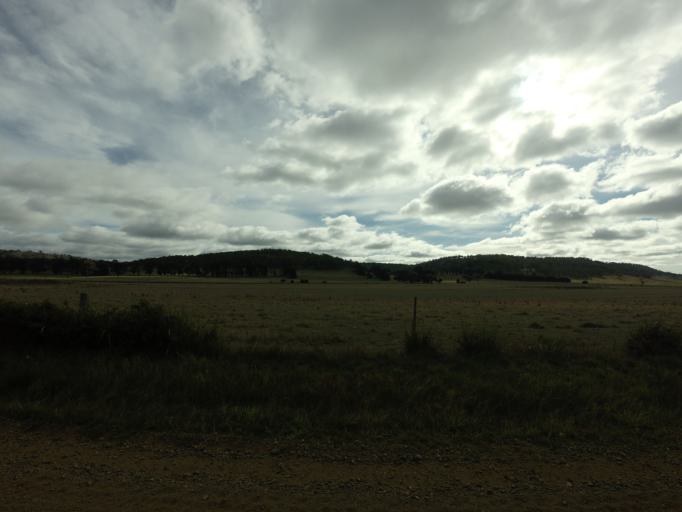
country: AU
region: Tasmania
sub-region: Brighton
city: Bridgewater
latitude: -42.3950
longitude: 147.3951
